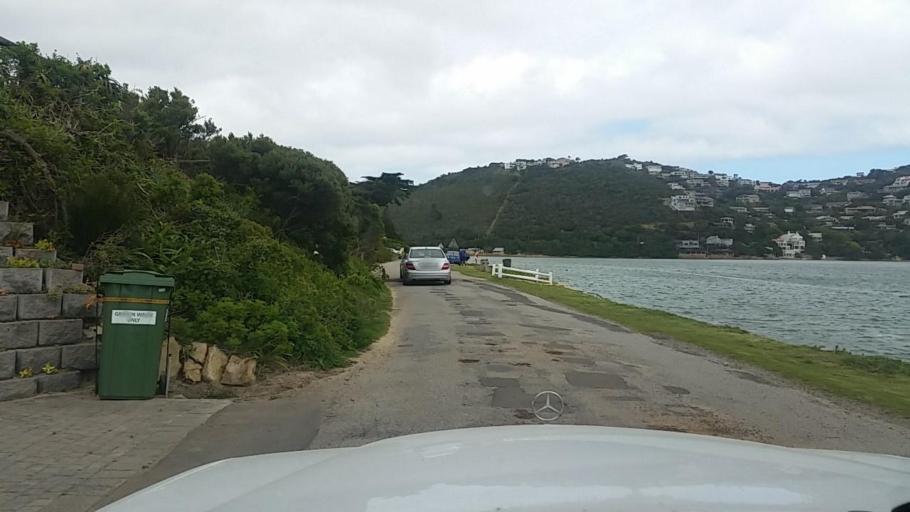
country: ZA
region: Western Cape
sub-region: Eden District Municipality
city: Knysna
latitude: -34.0698
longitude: 23.0596
